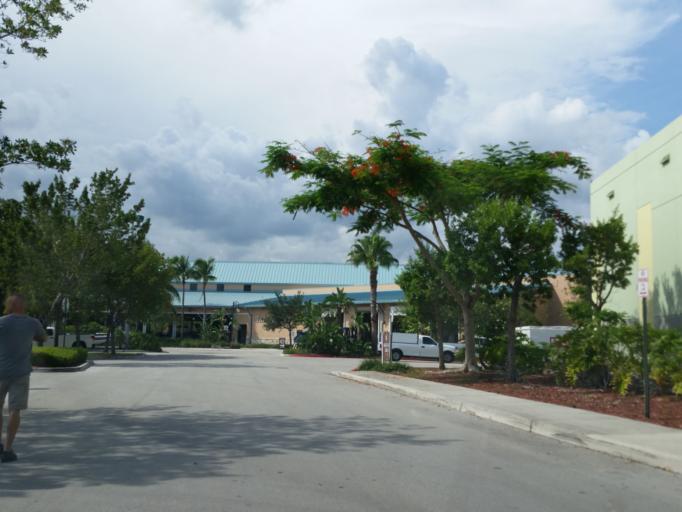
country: US
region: Florida
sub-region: Miami-Dade County
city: Sweetwater
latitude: 25.7878
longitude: -80.3836
